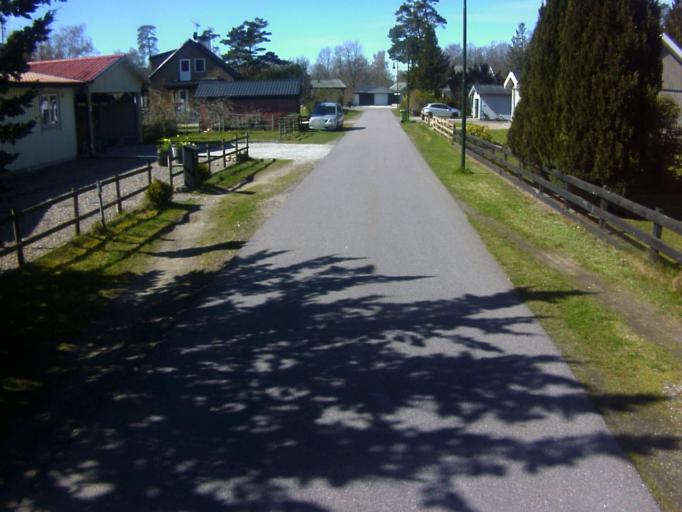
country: SE
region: Skane
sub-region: Kavlinge Kommun
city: Hofterup
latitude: 55.8117
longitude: 12.9803
